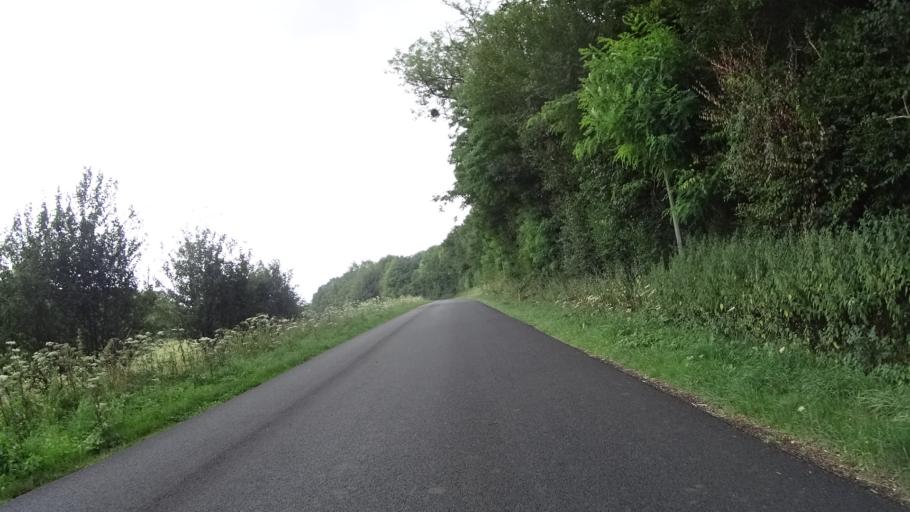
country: FR
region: Centre
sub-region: Departement du Loiret
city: Saint-Germain-des-Pres
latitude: 47.9261
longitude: 2.9002
